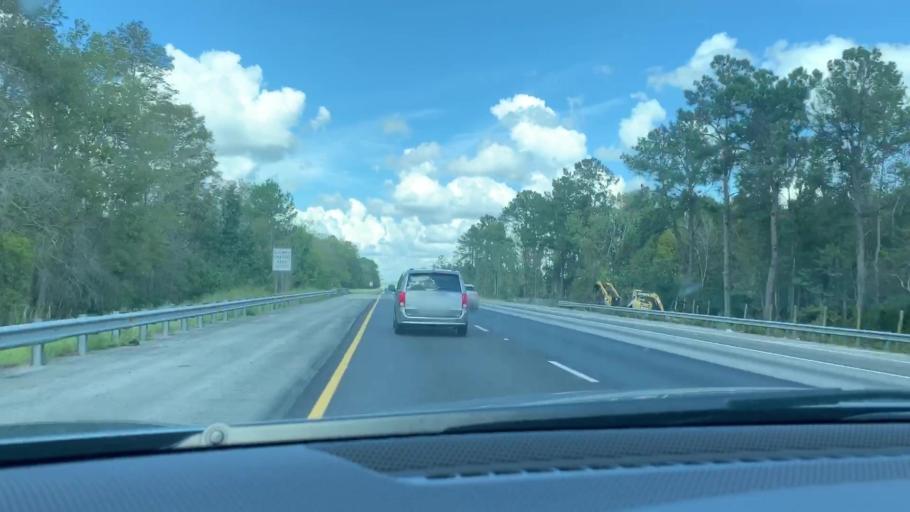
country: US
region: Georgia
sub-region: Camden County
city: Woodbine
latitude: 30.9114
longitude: -81.6859
